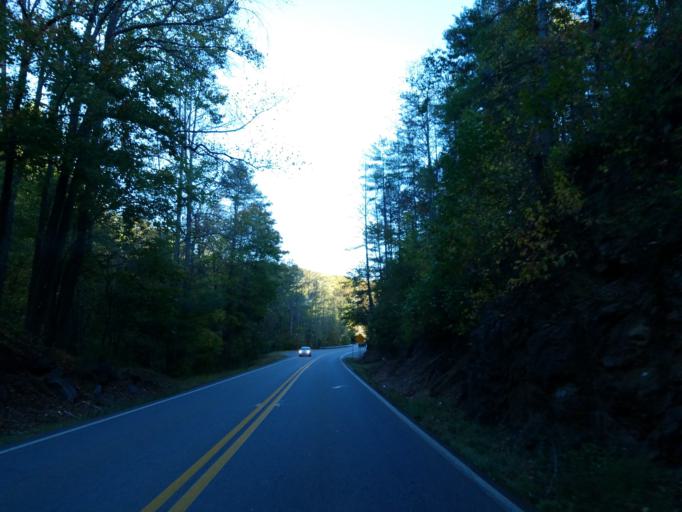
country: US
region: Georgia
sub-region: Dawson County
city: Dawsonville
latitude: 34.4273
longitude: -84.2148
